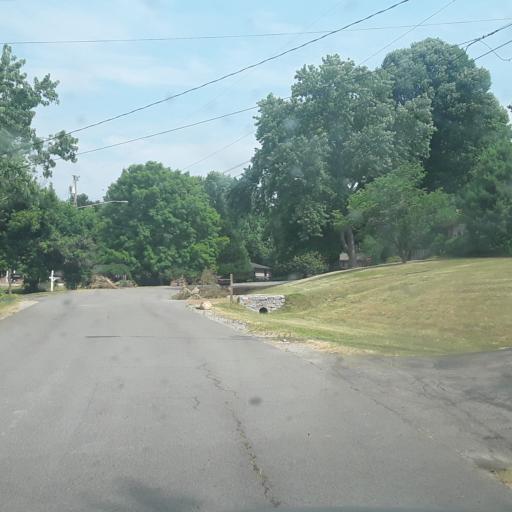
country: US
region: Tennessee
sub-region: Davidson County
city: Oak Hill
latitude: 36.0758
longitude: -86.7430
